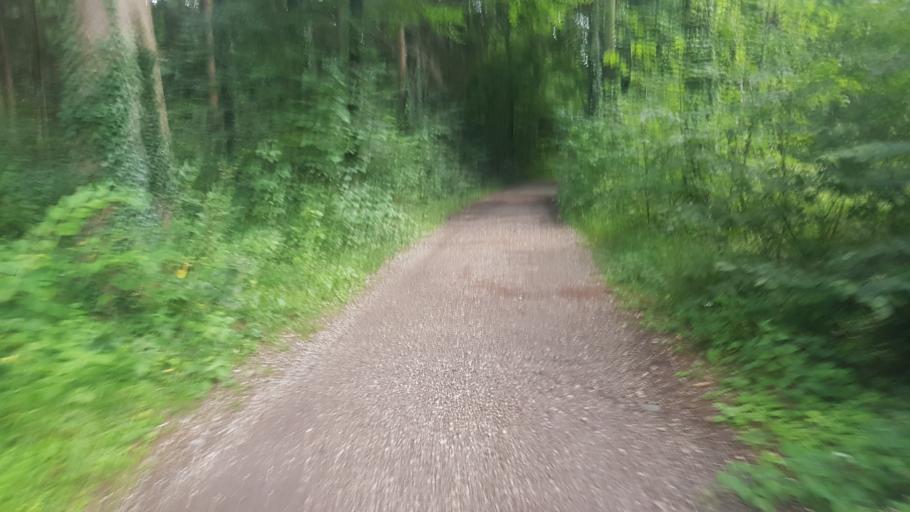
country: DE
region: Bavaria
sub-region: Upper Bavaria
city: Krailling
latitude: 48.0840
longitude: 11.3938
